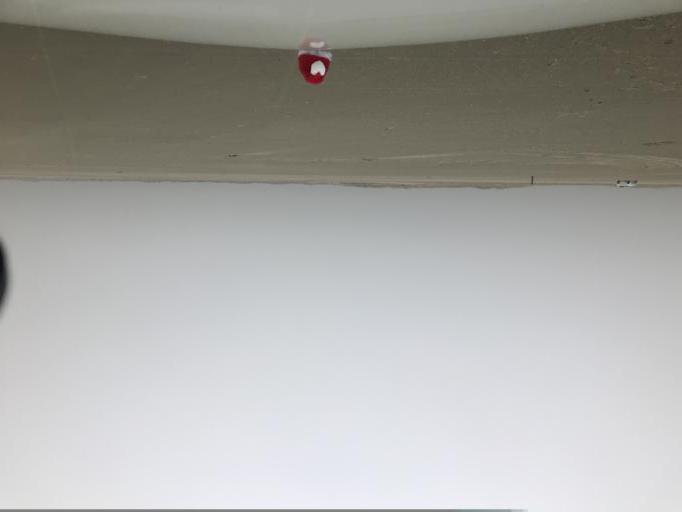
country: DE
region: Schleswig-Holstein
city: List
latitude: 55.1519
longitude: 8.4771
